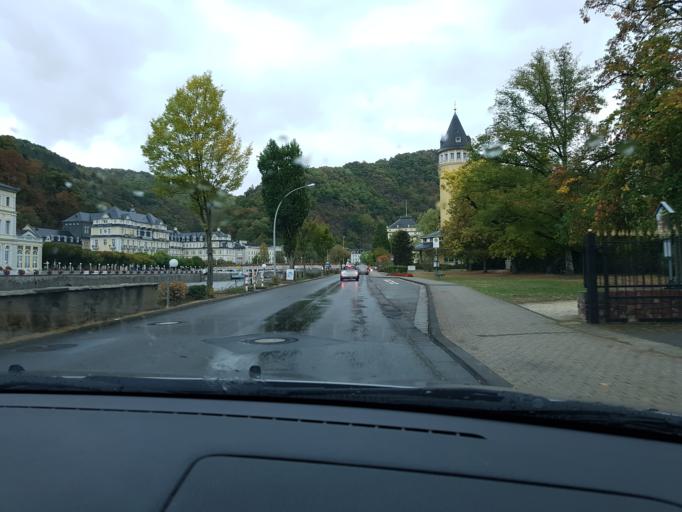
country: DE
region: Rheinland-Pfalz
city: Bad Ems
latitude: 50.3301
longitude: 7.7246
